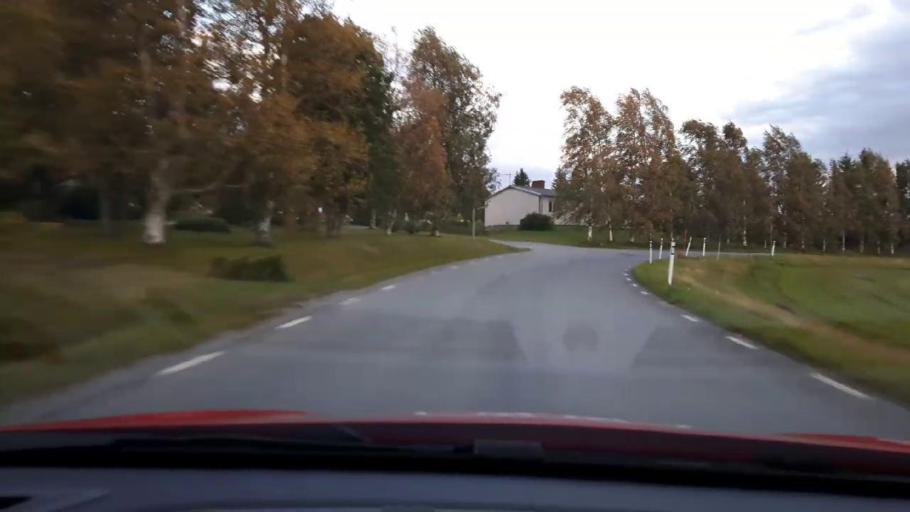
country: SE
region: Jaemtland
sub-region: Bergs Kommun
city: Hoverberg
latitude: 63.0294
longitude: 14.4736
